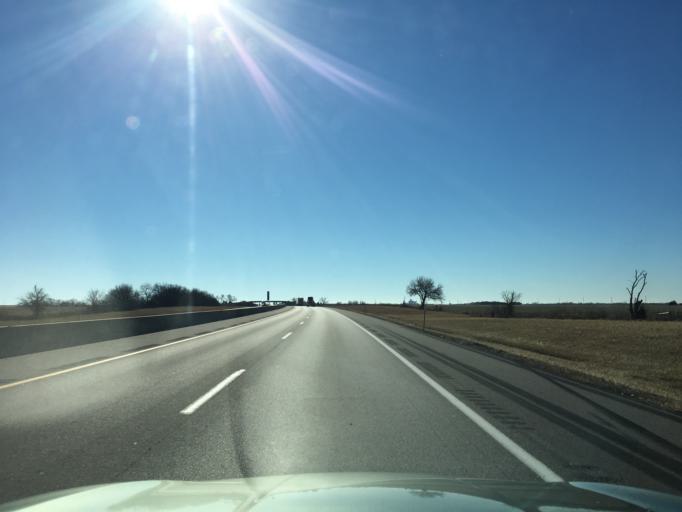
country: US
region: Kansas
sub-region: Sumner County
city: Wellington
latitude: 37.3122
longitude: -97.3404
